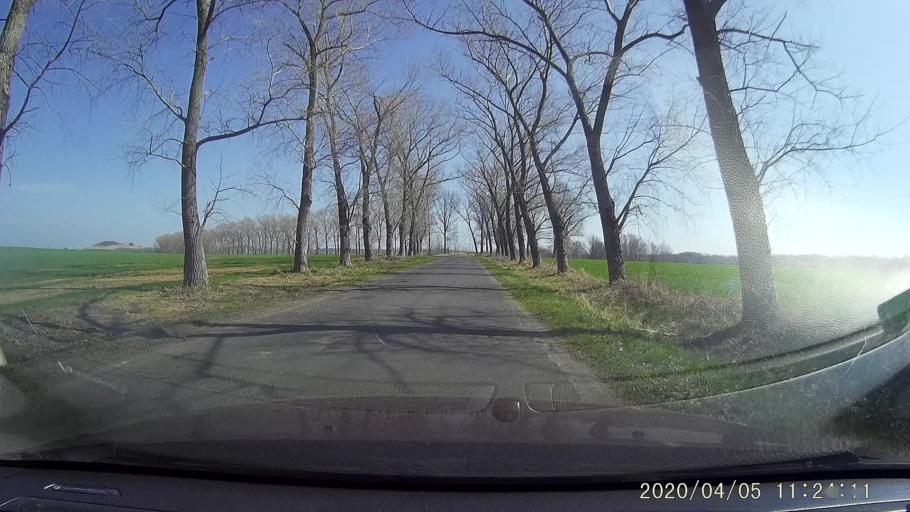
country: PL
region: Lower Silesian Voivodeship
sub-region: Powiat zgorzelecki
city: Sulikow
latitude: 51.0539
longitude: 15.1446
